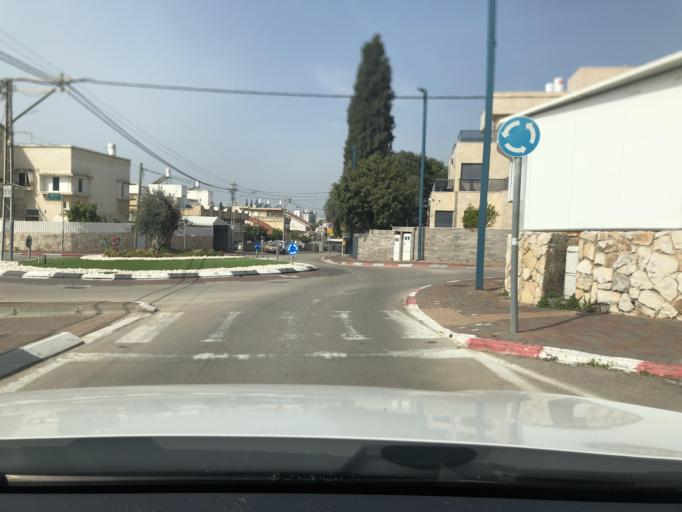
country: IL
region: Central District
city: Rosh Ha'Ayin
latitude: 32.0928
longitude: 34.9522
